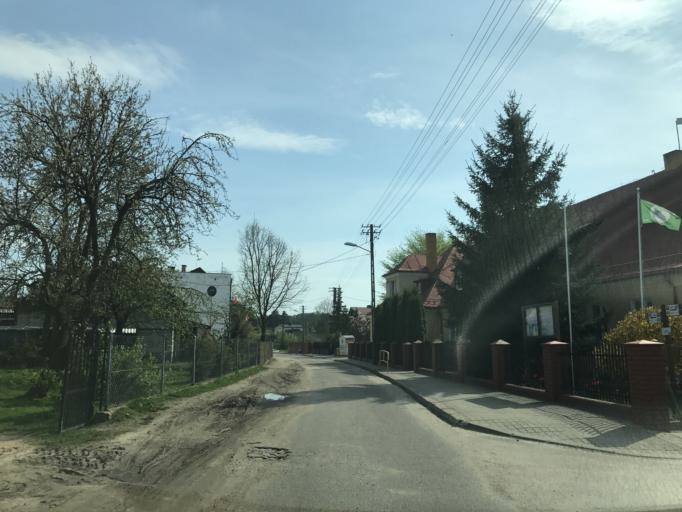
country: PL
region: Warmian-Masurian Voivodeship
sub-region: Powiat dzialdowski
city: Rybno
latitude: 53.3981
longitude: 19.8407
